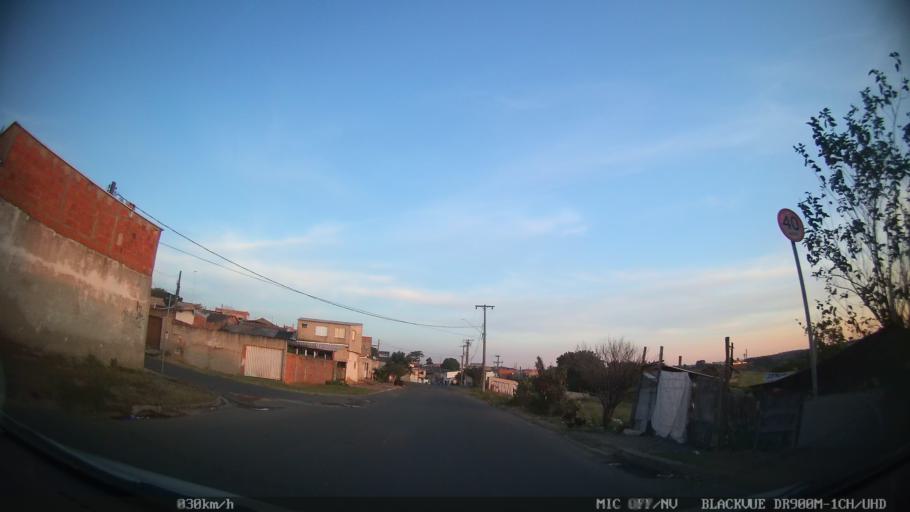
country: BR
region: Sao Paulo
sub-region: Campinas
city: Campinas
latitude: -22.9841
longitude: -47.1234
